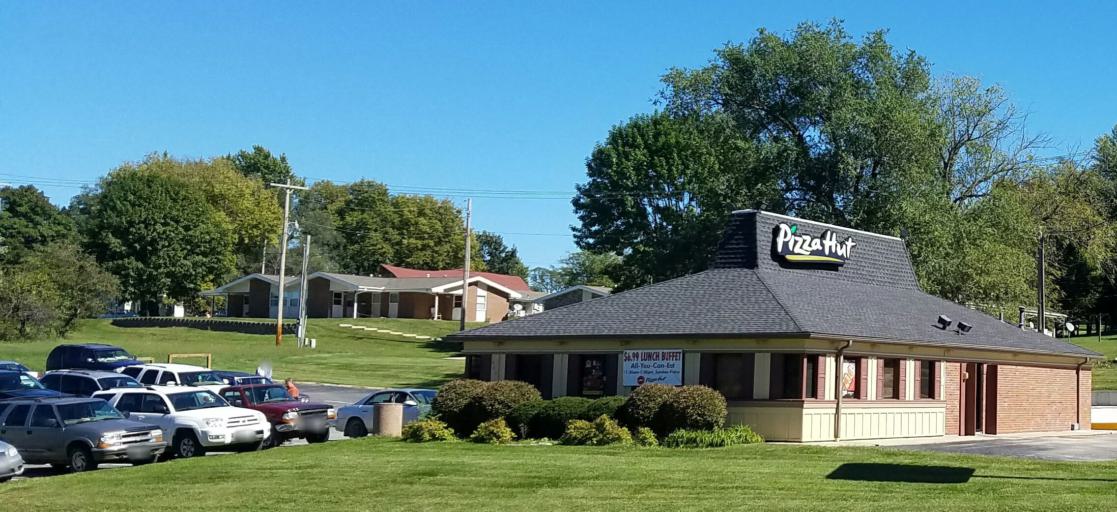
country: US
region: Missouri
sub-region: Harrison County
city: Bethany
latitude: 40.2670
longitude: -94.0273
